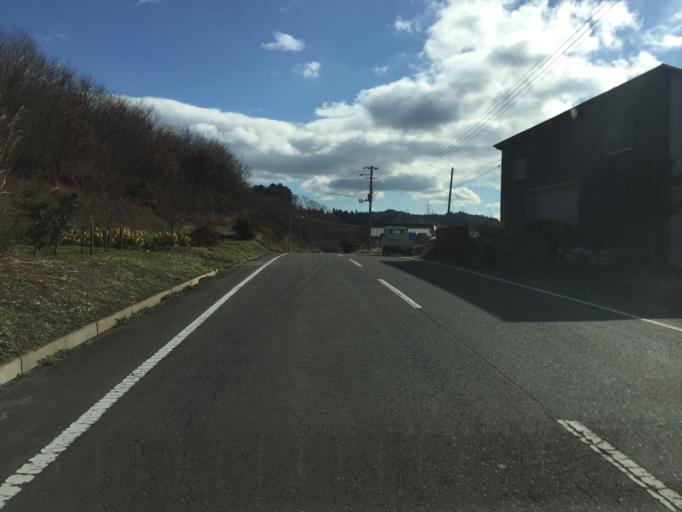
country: JP
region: Fukushima
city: Ishikawa
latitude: 37.2497
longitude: 140.5551
